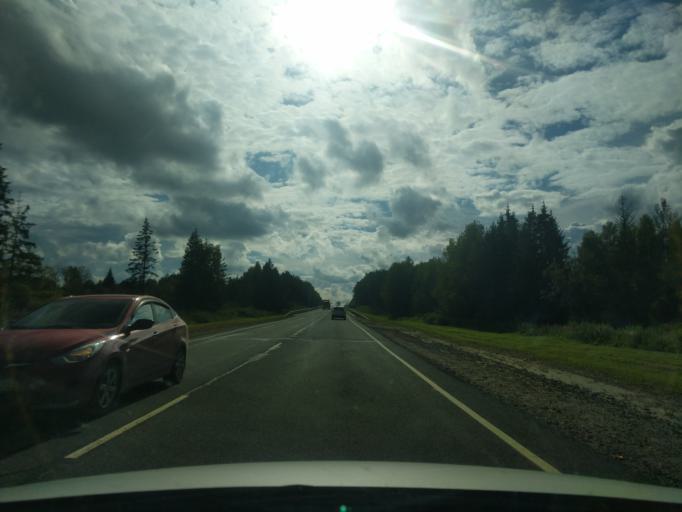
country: RU
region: Jaroslavl
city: Nekrasovskoye
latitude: 57.6214
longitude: 40.3580
